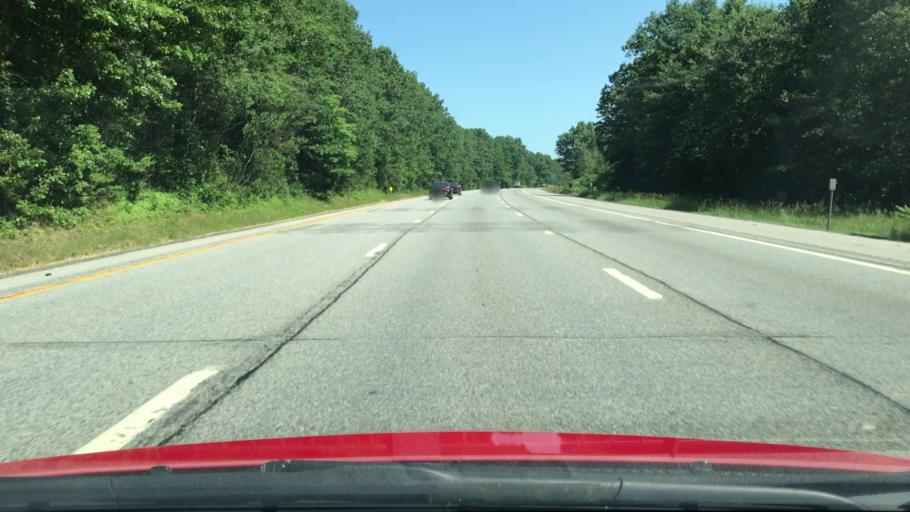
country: US
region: New York
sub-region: Saratoga County
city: Saratoga Springs
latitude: 43.1040
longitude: -73.7526
